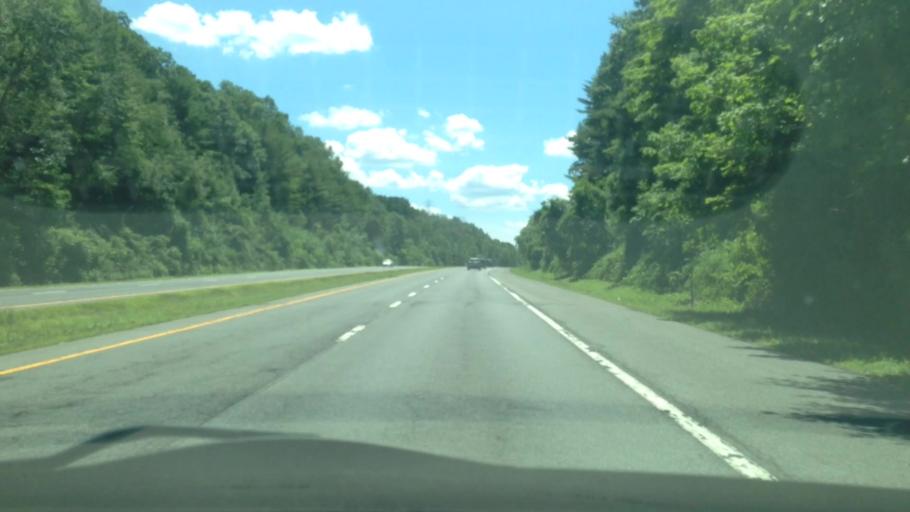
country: US
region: New York
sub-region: Ulster County
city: Lincoln Park
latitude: 41.9677
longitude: -74.0215
